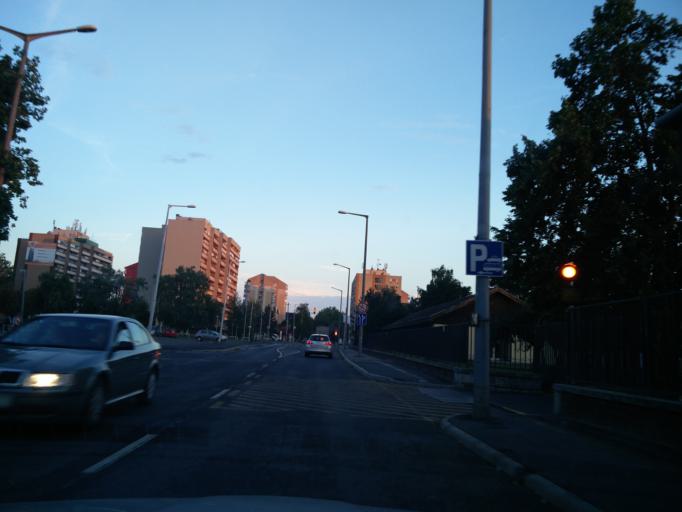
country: HU
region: Zala
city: Zalaegerszeg
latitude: 46.8466
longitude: 16.8511
